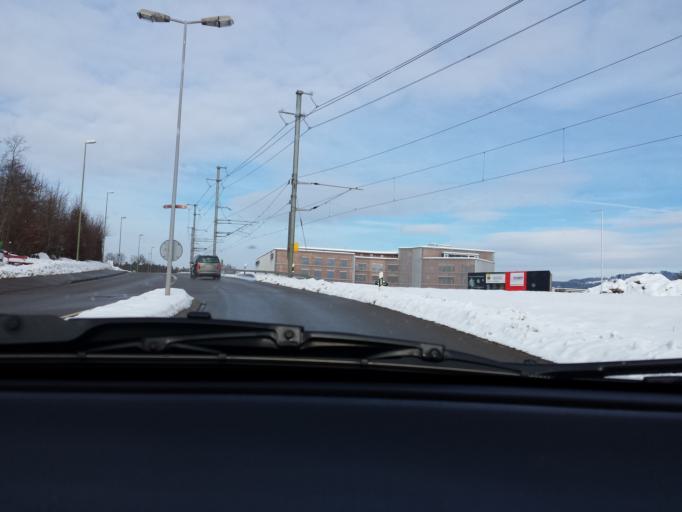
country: CH
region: Zurich
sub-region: Bezirk Hinwil
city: Bubikon
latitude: 47.2743
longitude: 8.8187
